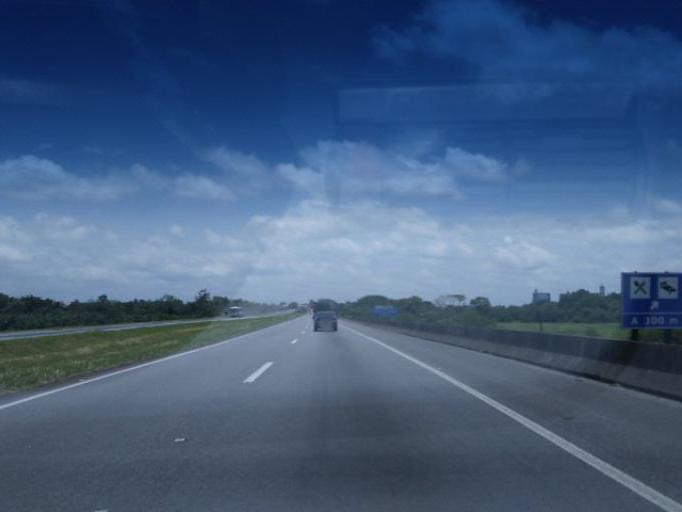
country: BR
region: Sao Paulo
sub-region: Registro
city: Registro
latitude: -24.4844
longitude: -47.8332
